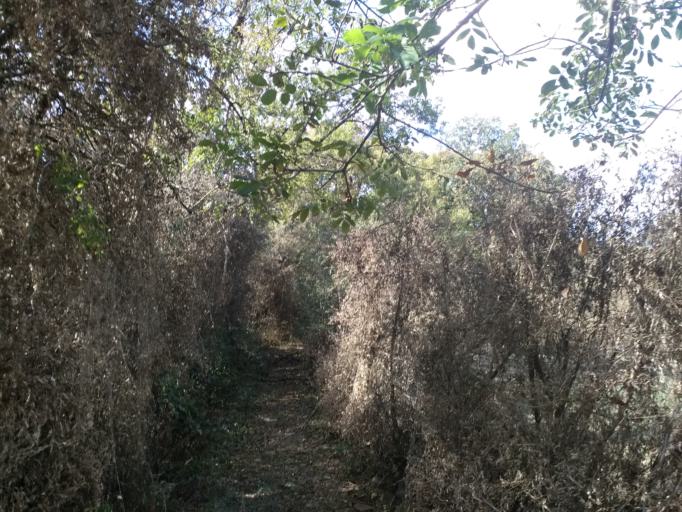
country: FR
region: Midi-Pyrenees
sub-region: Departement de l'Aveyron
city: Bozouls
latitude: 44.4618
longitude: 2.6872
